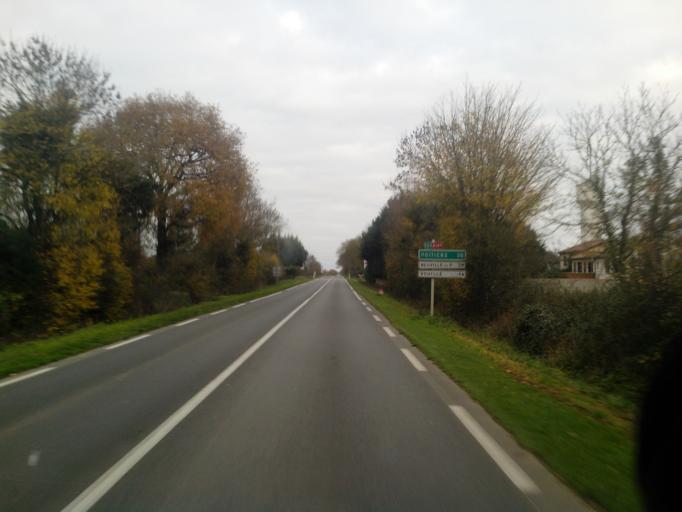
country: FR
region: Poitou-Charentes
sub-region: Departement des Deux-Sevres
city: Thenezay
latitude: 46.6553
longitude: -0.0710
